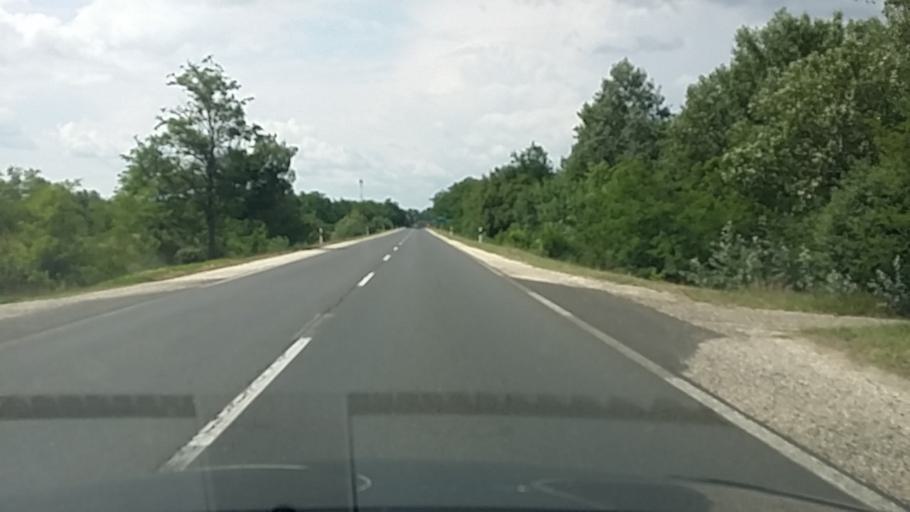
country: HU
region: Pest
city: Taborfalva
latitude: 47.0865
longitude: 19.4833
